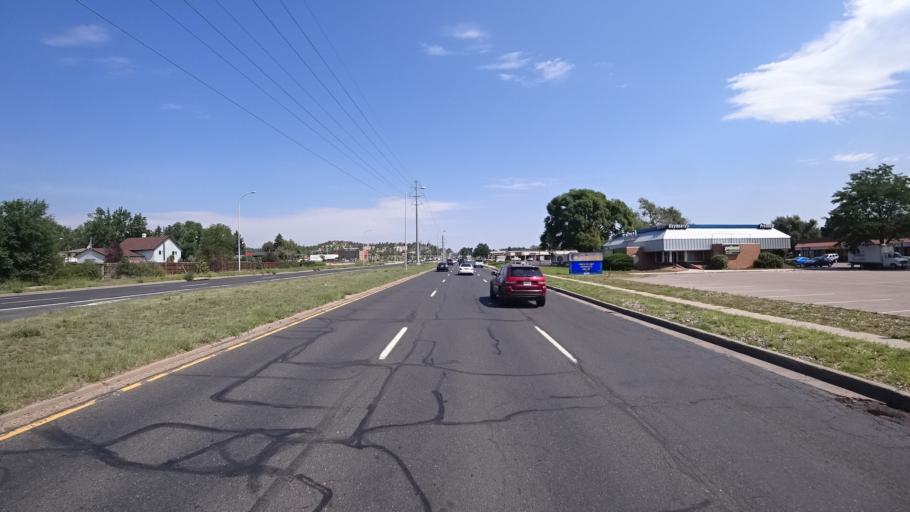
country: US
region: Colorado
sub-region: El Paso County
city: Cimarron Hills
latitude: 38.8647
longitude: -104.7570
